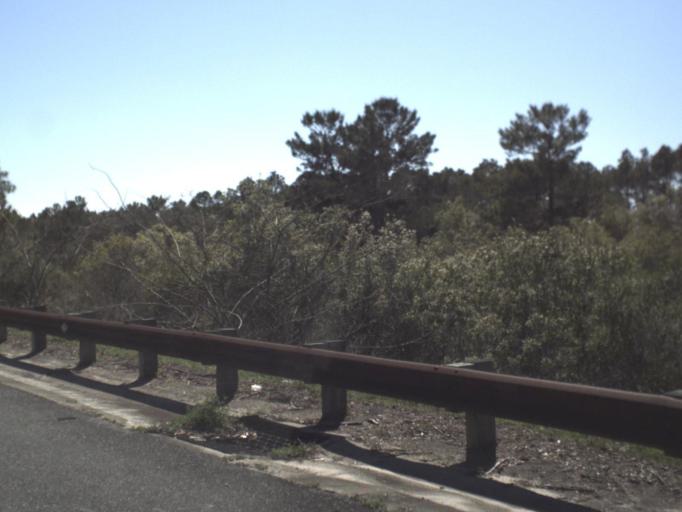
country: US
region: Florida
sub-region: Gulf County
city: Port Saint Joe
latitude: 29.8727
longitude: -85.3394
